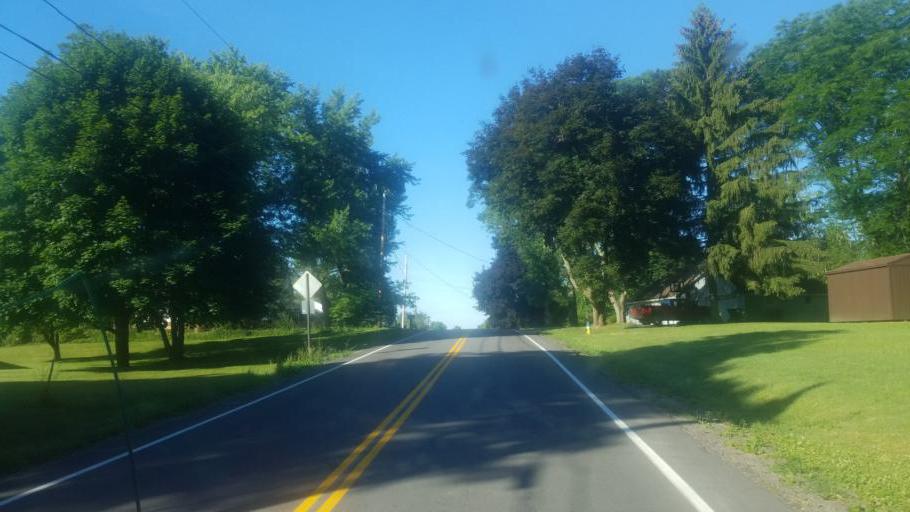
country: US
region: New York
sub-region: Wayne County
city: Newark
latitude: 43.0864
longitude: -77.0665
